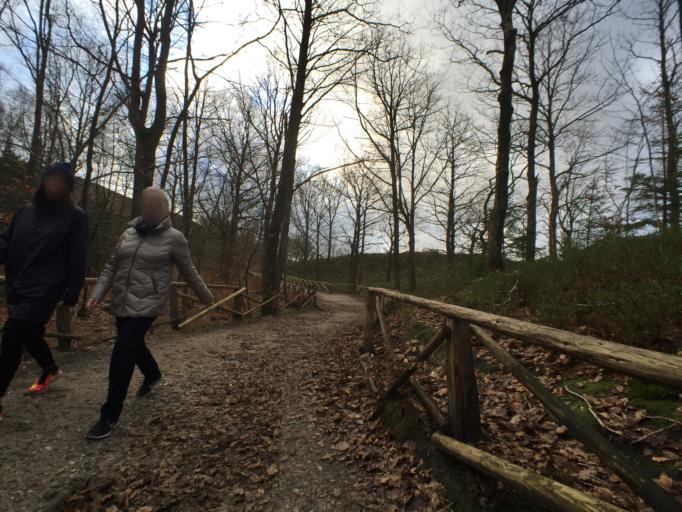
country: DK
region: Central Jutland
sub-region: Silkeborg Kommune
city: Svejbaek
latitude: 56.1081
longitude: 9.6847
